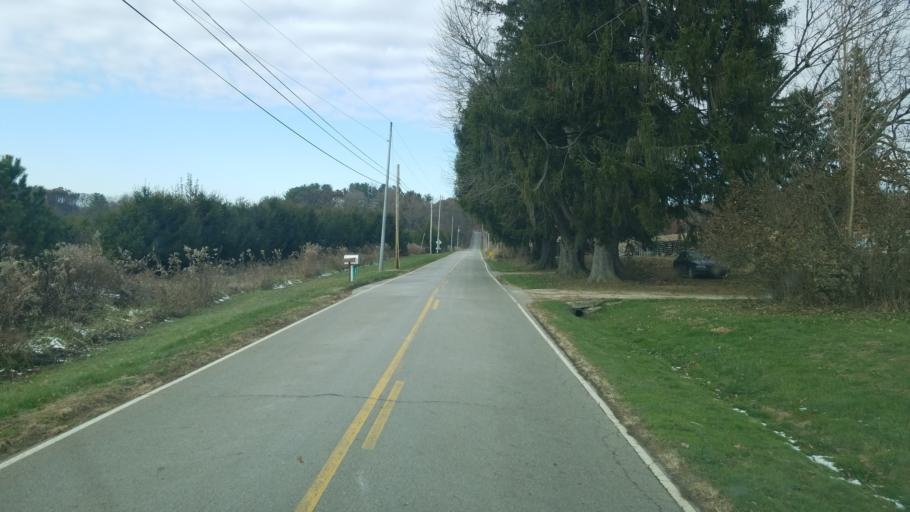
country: US
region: Ohio
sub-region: Licking County
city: Newark
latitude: 40.1532
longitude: -82.3756
